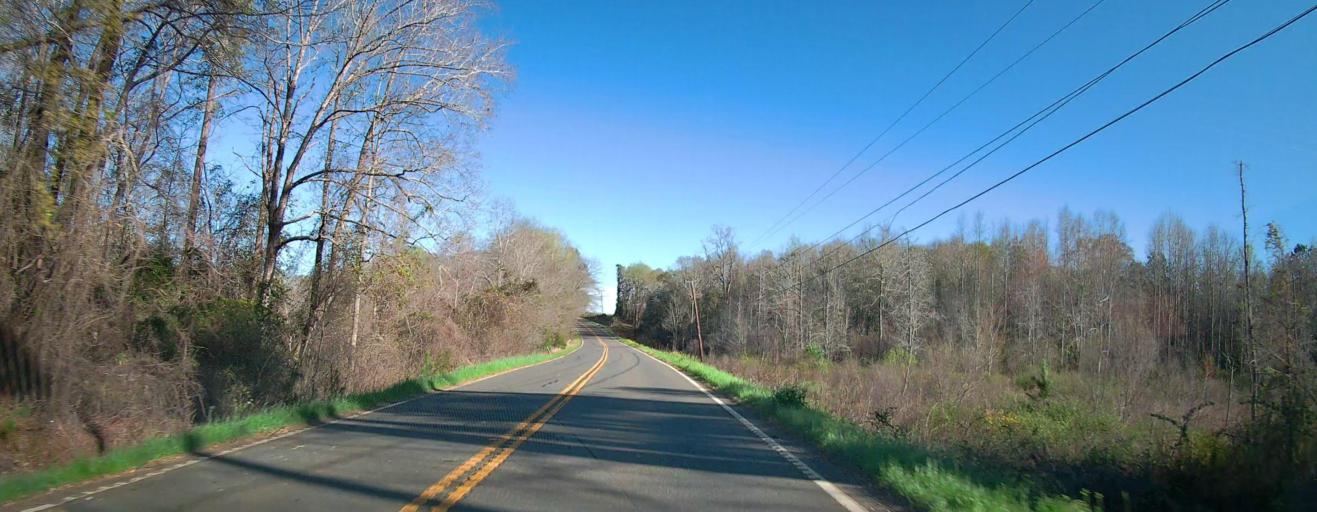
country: US
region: Georgia
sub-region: Macon County
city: Marshallville
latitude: 32.4493
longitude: -83.9083
